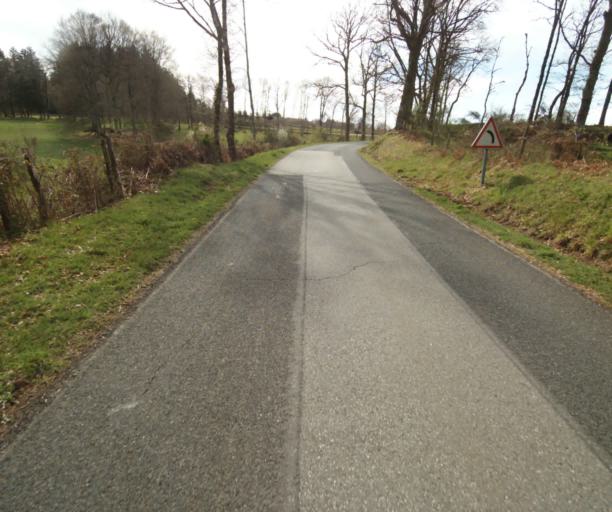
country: FR
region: Limousin
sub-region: Departement de la Correze
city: Correze
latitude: 45.3703
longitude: 1.9056
